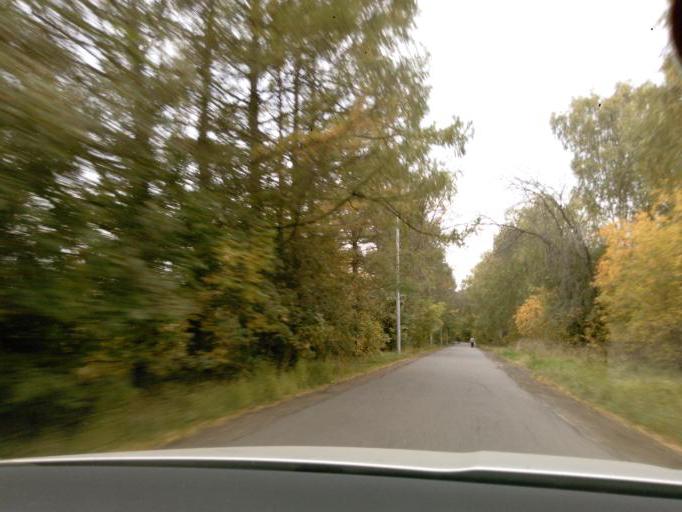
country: RU
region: Moscow
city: Severnyy
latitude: 55.9413
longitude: 37.5272
